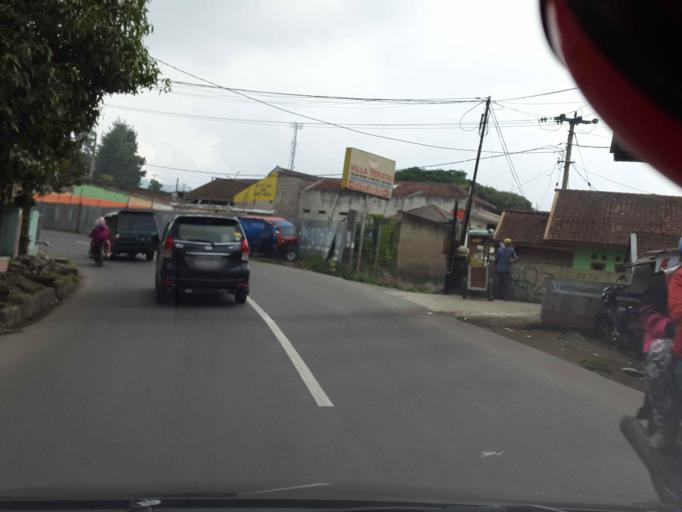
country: ID
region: West Java
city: Lembang
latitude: -6.8086
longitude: 107.6468
